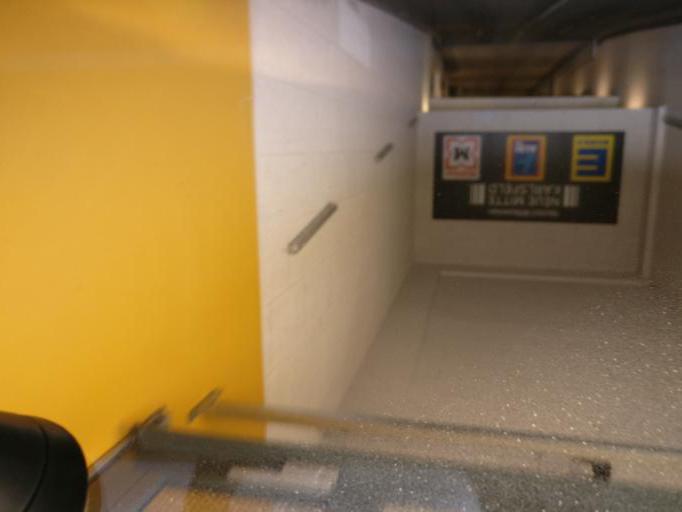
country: DE
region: Bavaria
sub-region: Upper Bavaria
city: Karlsfeld
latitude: 48.2267
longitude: 11.4703
